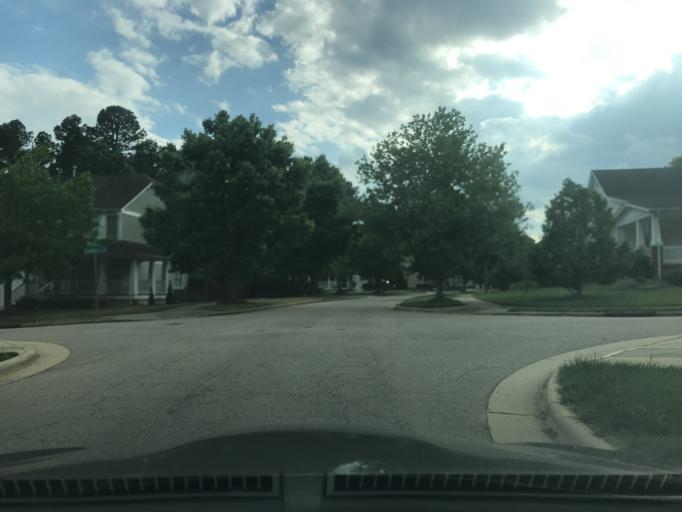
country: US
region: North Carolina
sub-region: Wake County
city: Wake Forest
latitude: 35.9173
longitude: -78.5660
